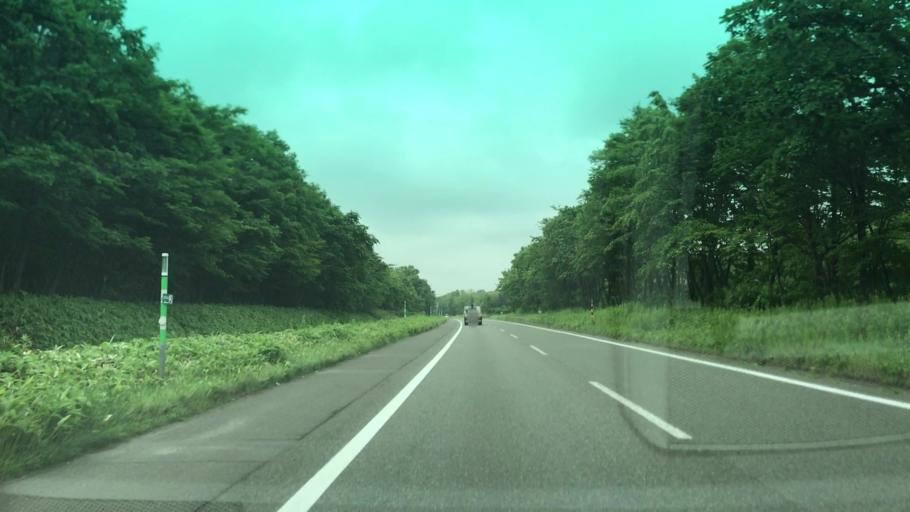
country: JP
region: Hokkaido
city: Chitose
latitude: 42.7428
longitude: 141.6501
